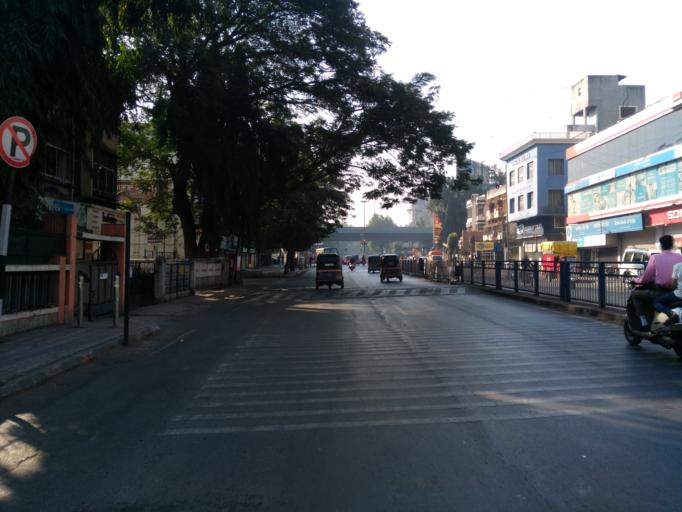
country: IN
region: Maharashtra
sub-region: Pune Division
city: Pune
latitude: 18.5028
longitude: 73.8690
